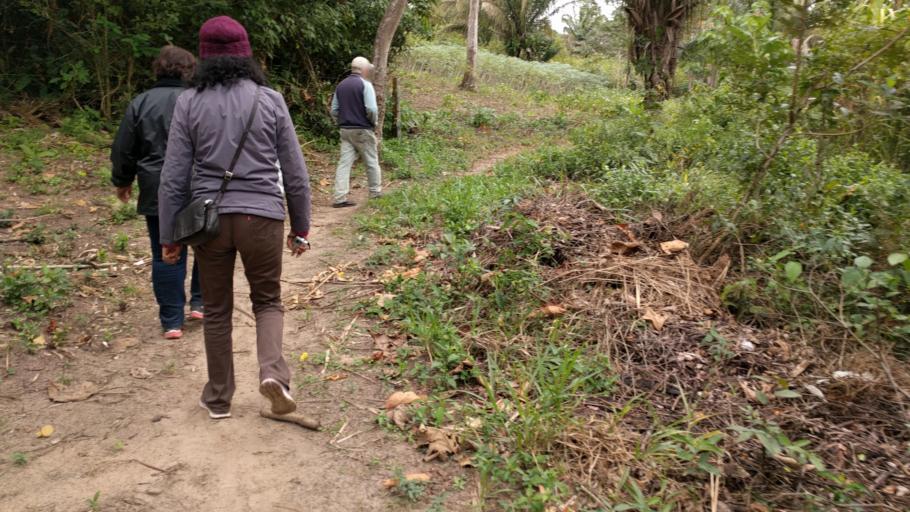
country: BO
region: Santa Cruz
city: San Juan del Surutu
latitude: -17.4584
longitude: -63.6960
